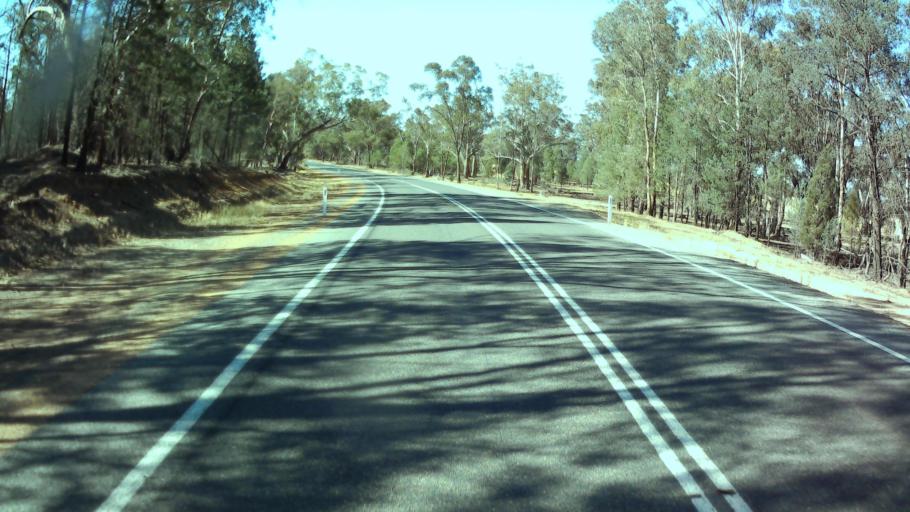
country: AU
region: New South Wales
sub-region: Weddin
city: Grenfell
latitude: -33.7449
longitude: 148.0883
